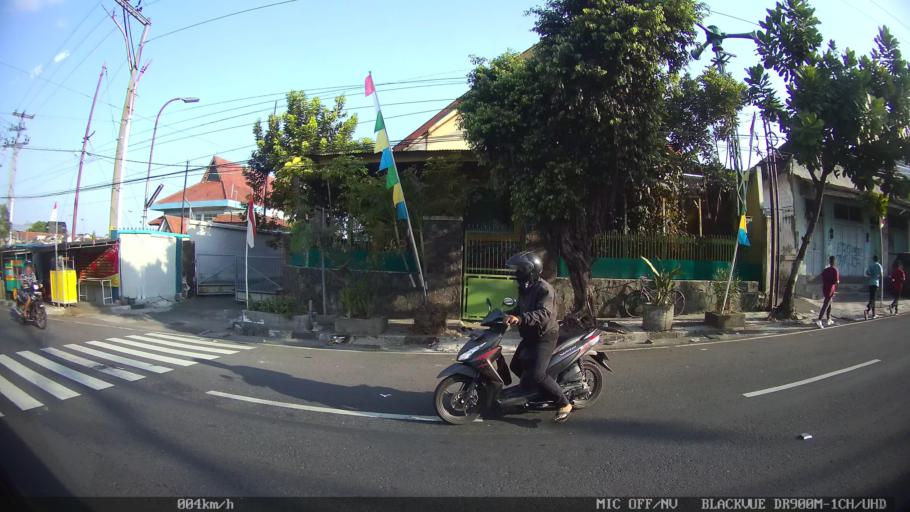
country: ID
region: Daerah Istimewa Yogyakarta
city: Yogyakarta
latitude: -7.8013
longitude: 110.3537
